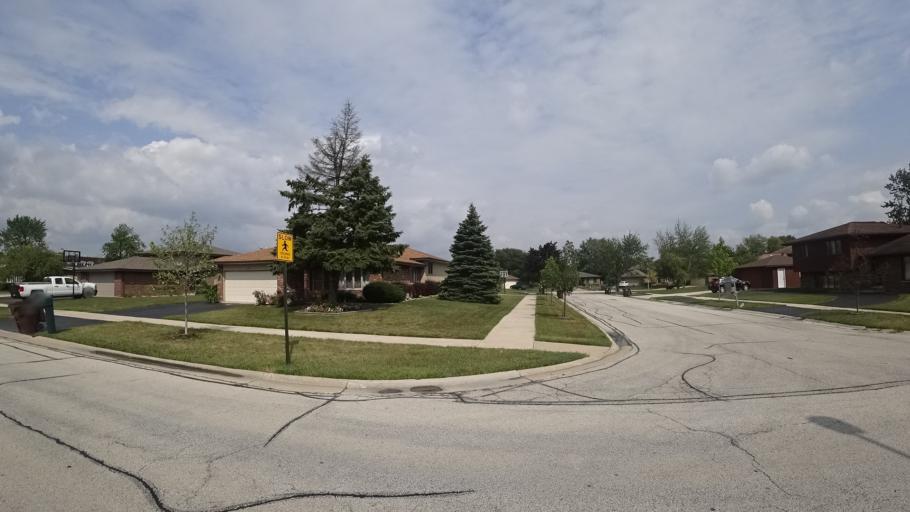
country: US
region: Illinois
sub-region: Cook County
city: Tinley Park
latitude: 41.5932
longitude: -87.7918
